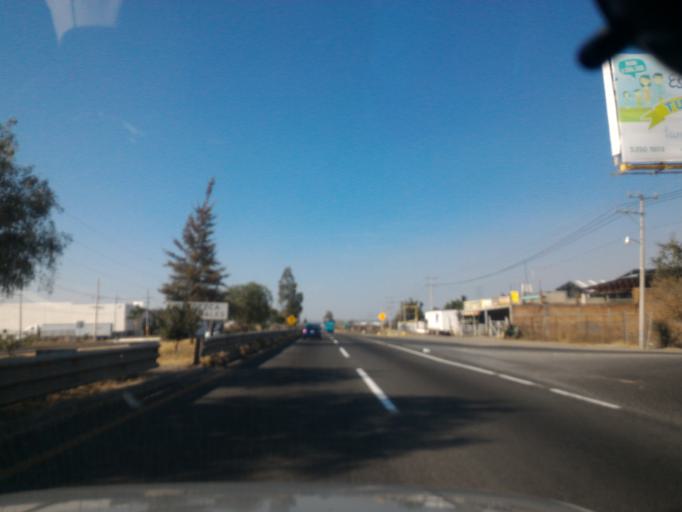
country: MX
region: Jalisco
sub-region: Ixtlahuacan de los Membrillos
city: Los Olivos
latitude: 20.4365
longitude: -103.2426
